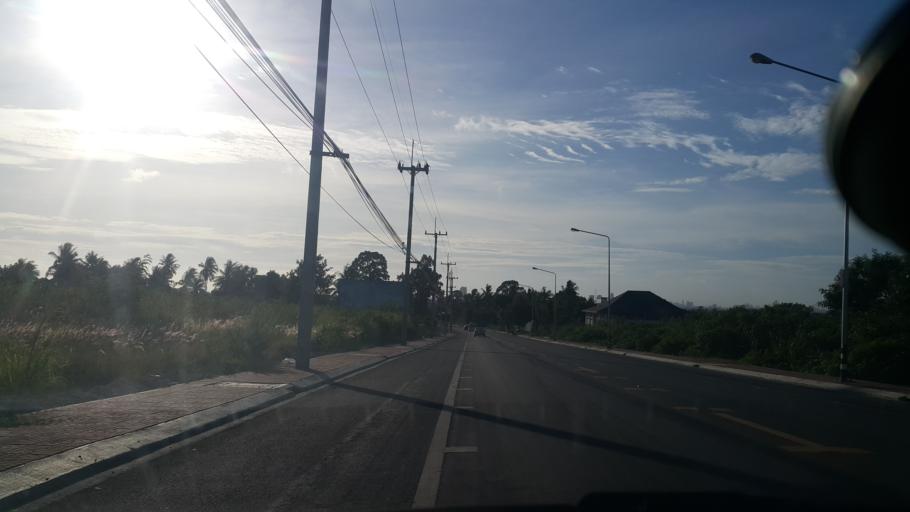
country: TH
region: Rayong
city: Ban Chang
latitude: 12.7720
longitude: 100.9502
